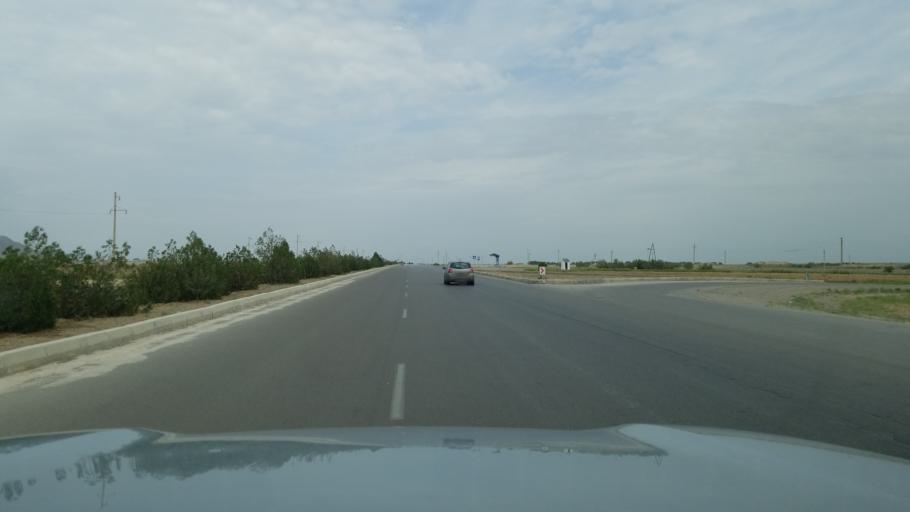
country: TM
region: Ahal
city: Arcabil
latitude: 38.2201
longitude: 57.8017
